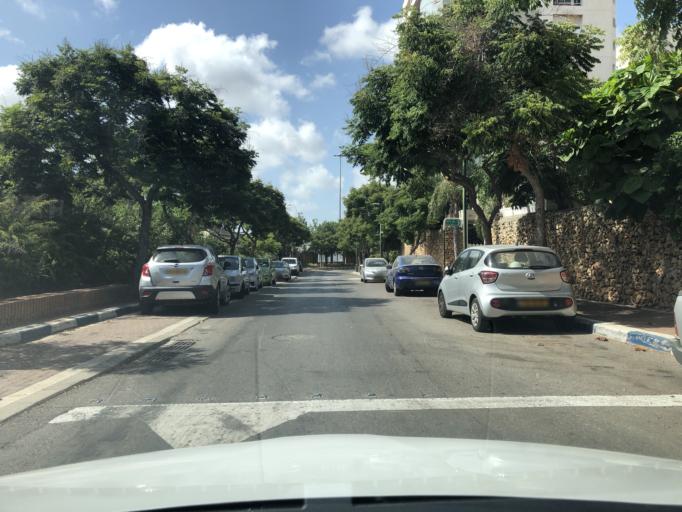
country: IL
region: Tel Aviv
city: Giv`at Shemu'el
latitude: 32.0639
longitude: 34.8458
